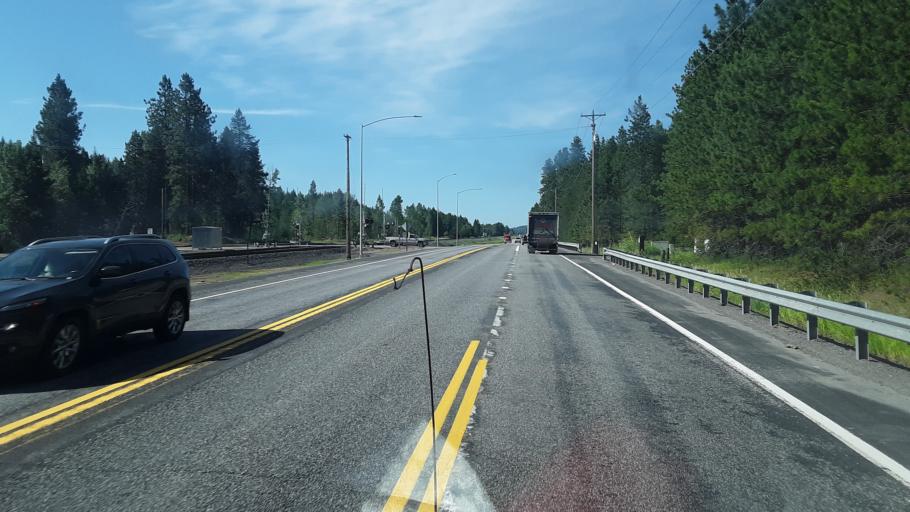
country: US
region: Idaho
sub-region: Bonner County
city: Ponderay
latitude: 48.4860
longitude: -116.4600
